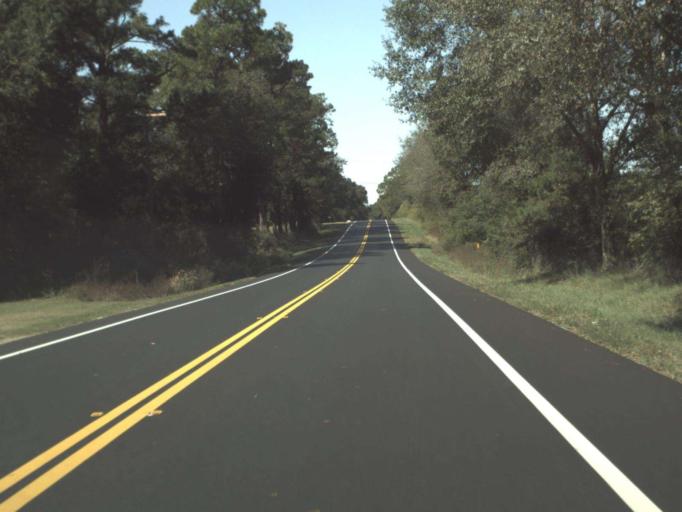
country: US
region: Florida
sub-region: Walton County
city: DeFuniak Springs
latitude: 30.8186
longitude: -86.2102
